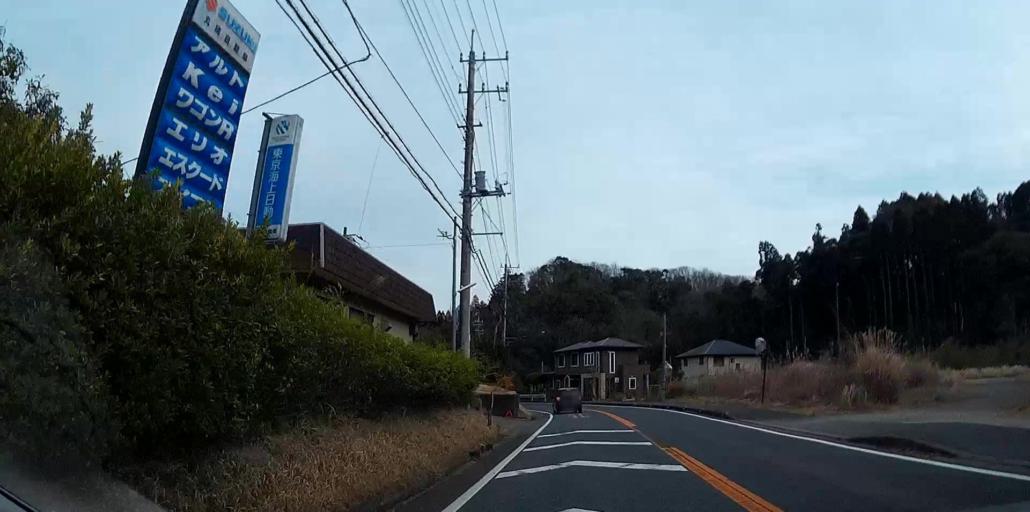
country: JP
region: Chiba
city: Kawaguchi
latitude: 35.2675
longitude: 140.0615
